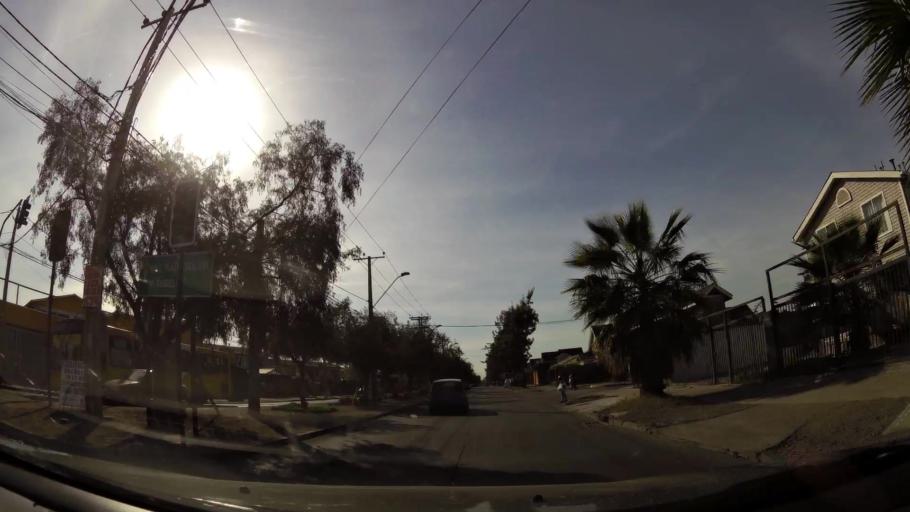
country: CL
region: Santiago Metropolitan
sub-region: Provincia de Cordillera
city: Puente Alto
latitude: -33.5923
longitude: -70.5604
